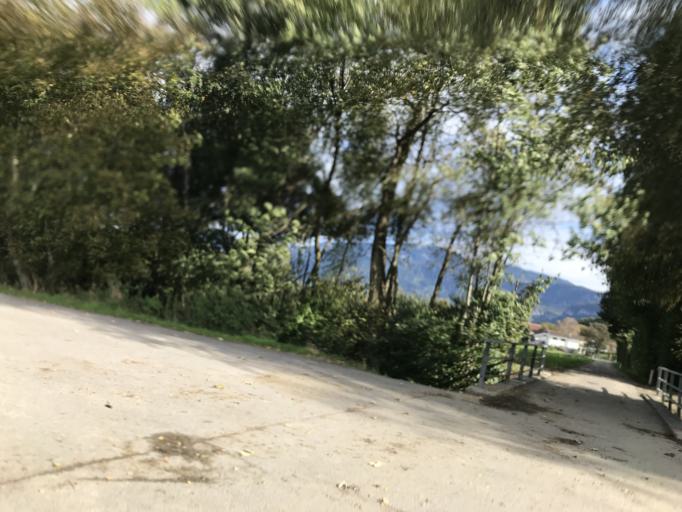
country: AT
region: Vorarlberg
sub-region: Politischer Bezirk Feldkirch
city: Mader
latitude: 47.3470
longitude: 9.6041
